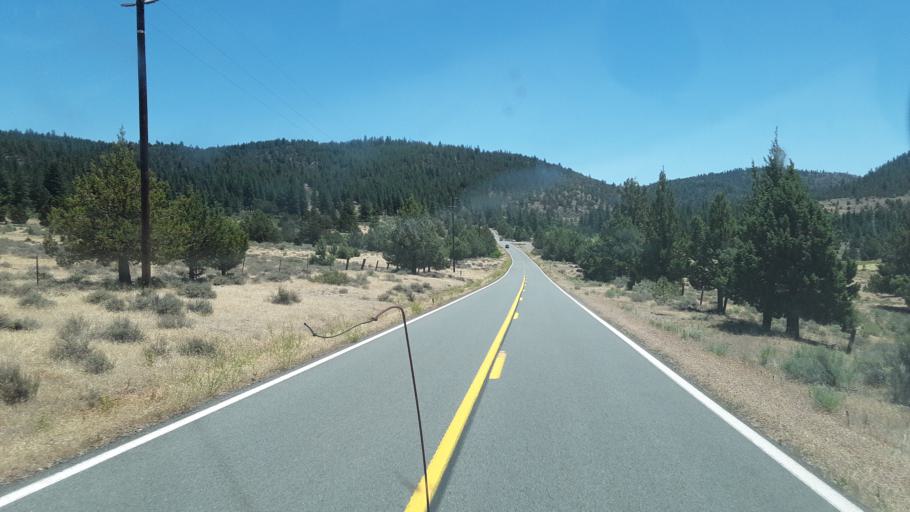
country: US
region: California
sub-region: Modoc County
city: Alturas
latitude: 41.0409
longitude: -120.8619
